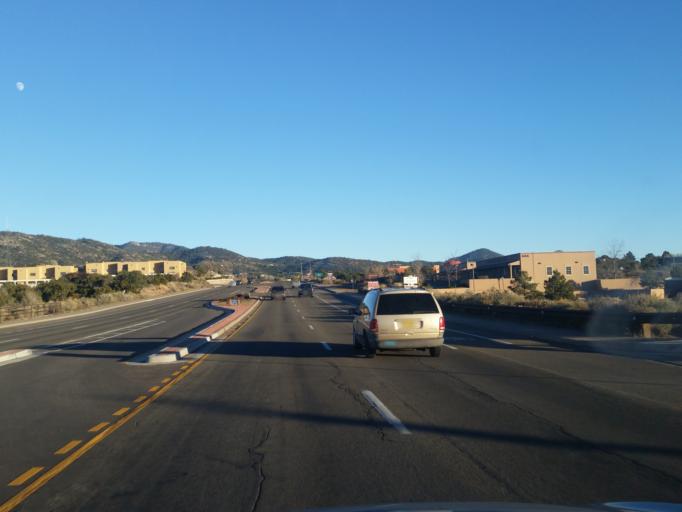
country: US
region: New Mexico
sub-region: Santa Fe County
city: Santa Fe
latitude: 35.6573
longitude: -105.9458
